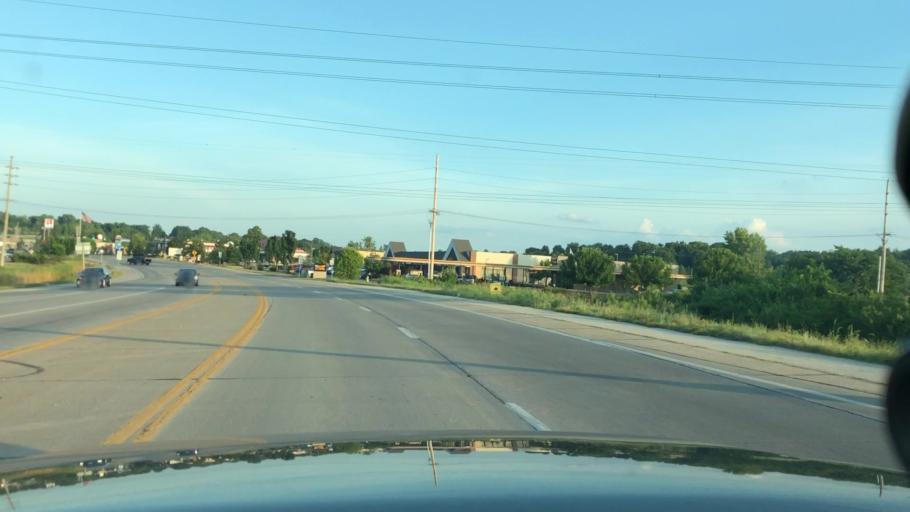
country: US
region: Missouri
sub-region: Saint Charles County
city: Saint Charles
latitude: 38.8233
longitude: -90.5179
